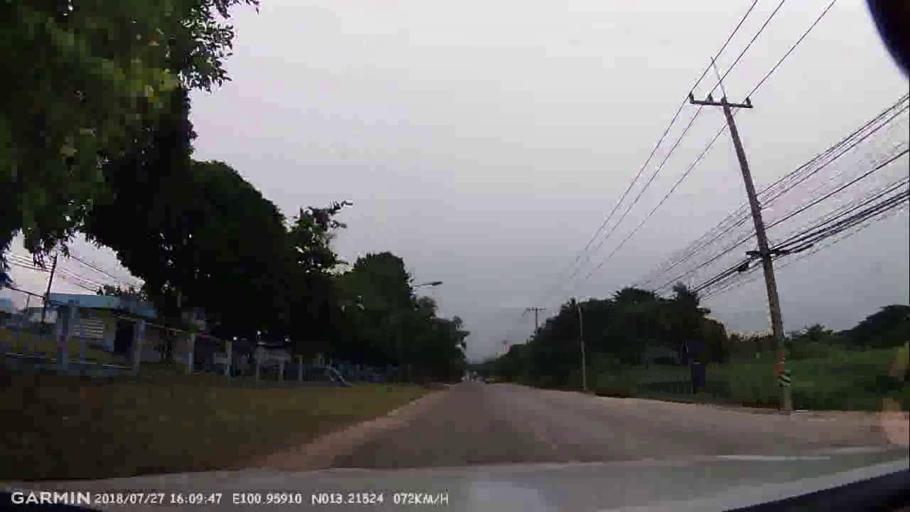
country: TH
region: Chon Buri
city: Si Racha
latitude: 13.2152
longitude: 100.9592
